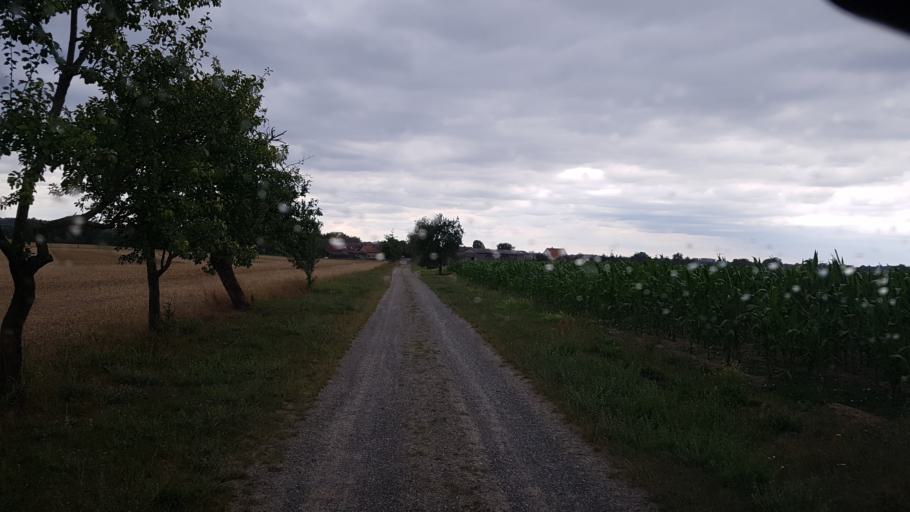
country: DE
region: Brandenburg
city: Sonnewalde
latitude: 51.7105
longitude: 13.7001
